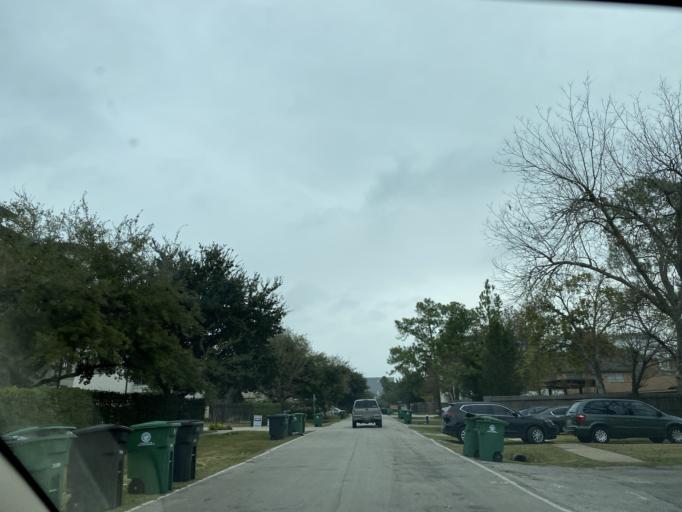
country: US
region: Texas
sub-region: Harris County
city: Bellaire
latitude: 29.7343
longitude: -95.4797
